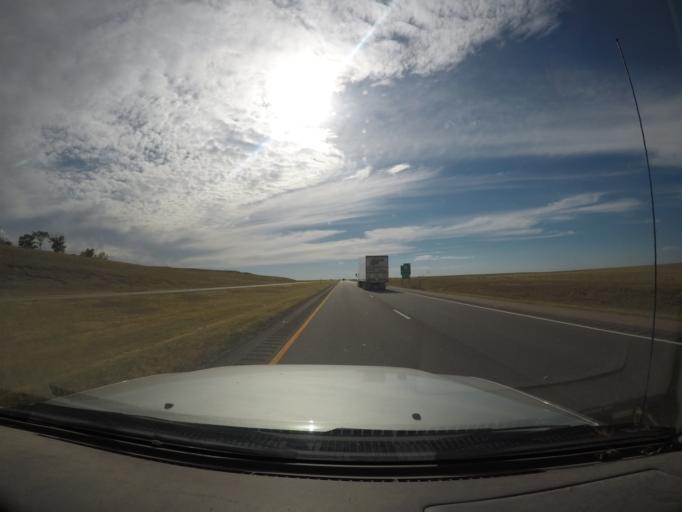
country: US
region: Wyoming
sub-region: Laramie County
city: Pine Bluffs
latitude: 41.1910
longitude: -103.8685
